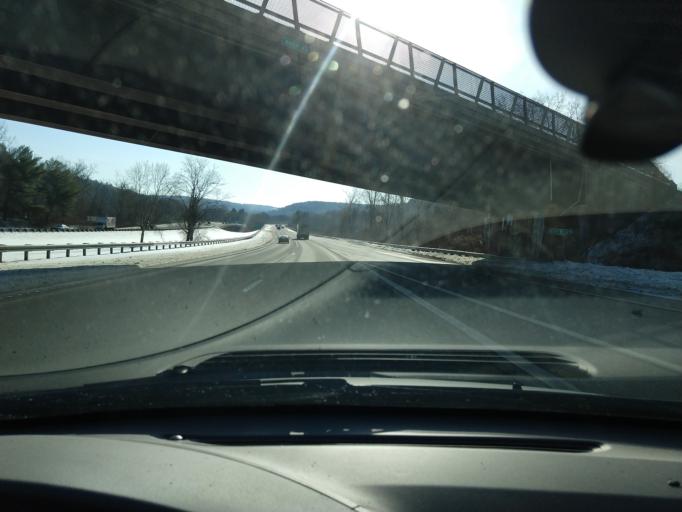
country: US
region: Connecticut
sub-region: New Haven County
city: Heritage Village
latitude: 41.4423
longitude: -73.2496
